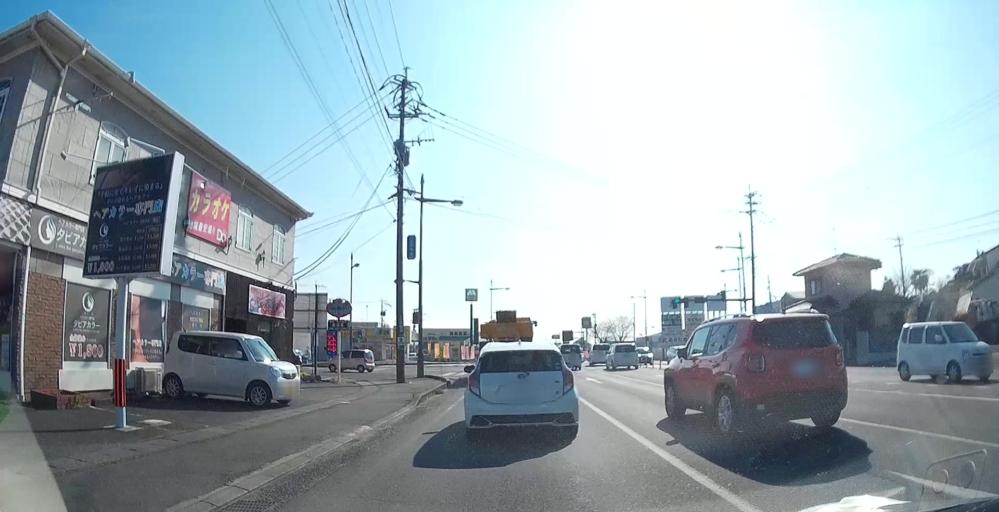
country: JP
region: Kumamoto
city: Kumamoto
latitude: 32.7841
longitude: 130.6734
